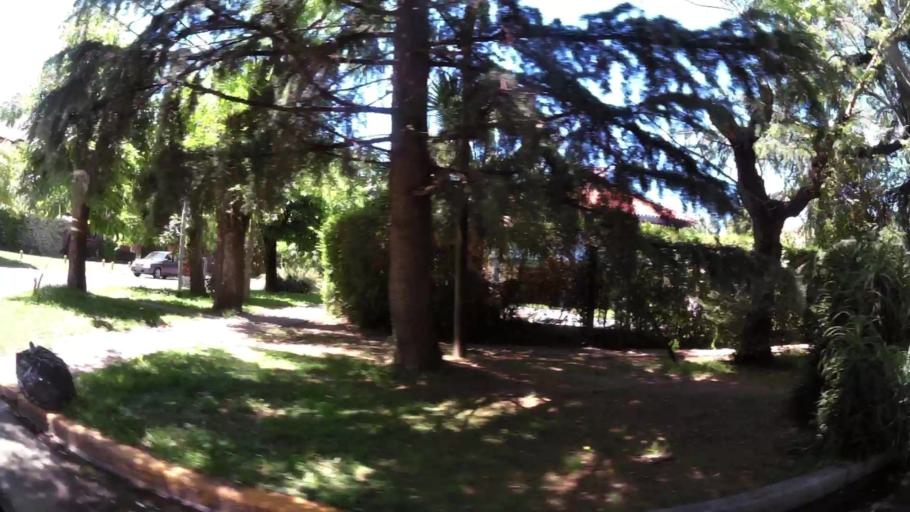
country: AR
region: Buenos Aires
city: Hurlingham
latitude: -34.4965
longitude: -58.6405
